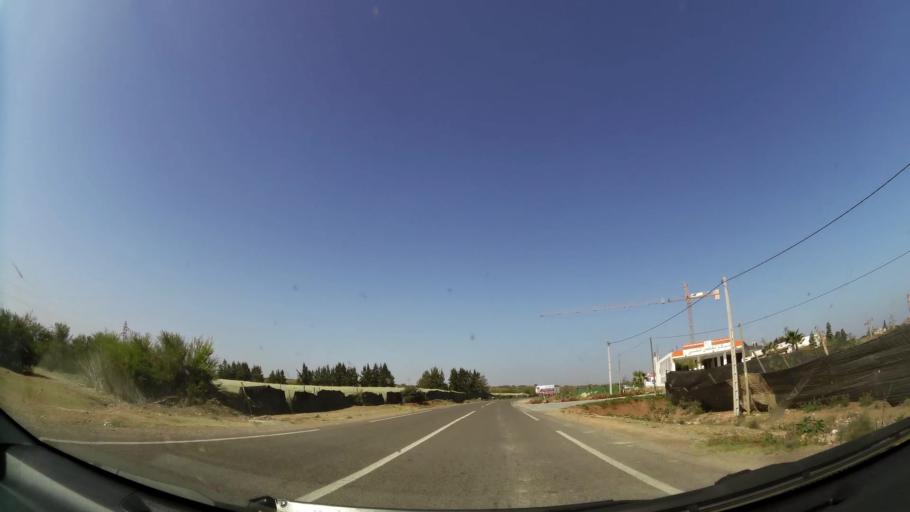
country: MA
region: Souss-Massa-Draa
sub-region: Inezgane-Ait Mellou
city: Inezgane
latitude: 30.3090
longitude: -9.5045
